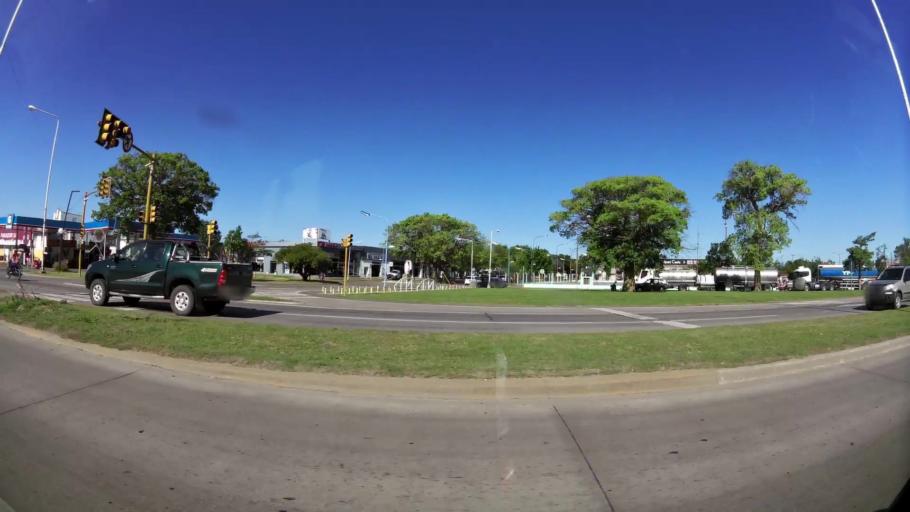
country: AR
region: Santa Fe
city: Rafaela
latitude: -31.2510
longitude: -61.5058
